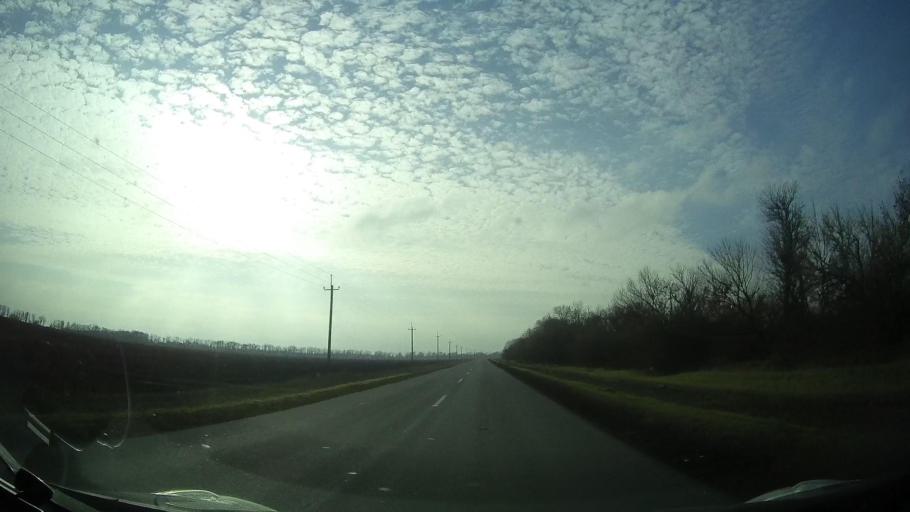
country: RU
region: Rostov
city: Mechetinskaya
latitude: 46.7937
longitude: 40.4995
